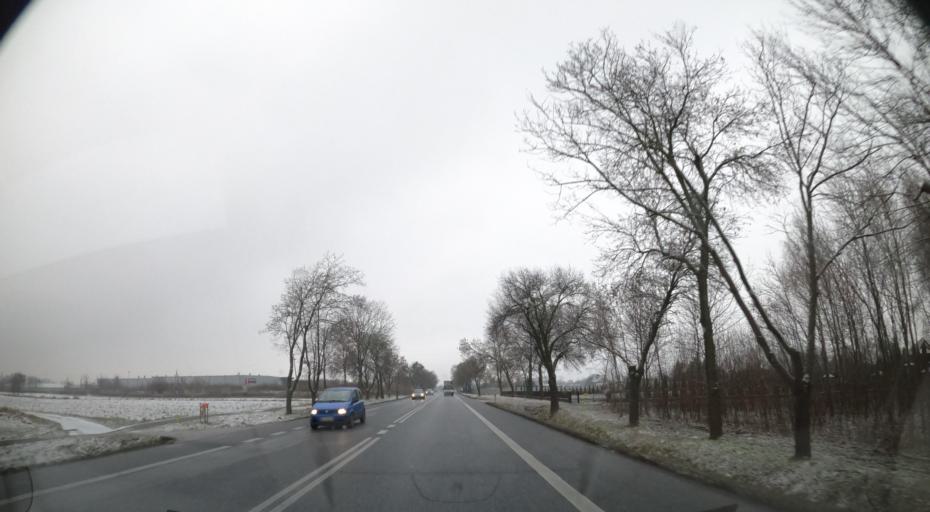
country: PL
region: Masovian Voivodeship
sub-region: Powiat warszawski zachodni
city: Bieniewice
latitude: 52.2034
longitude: 20.5236
